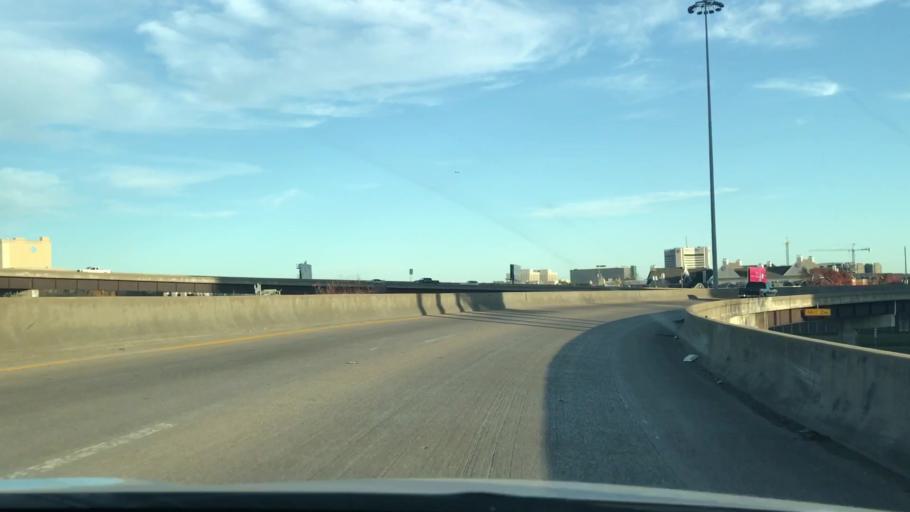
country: US
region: Texas
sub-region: Dallas County
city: Dallas
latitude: 32.7940
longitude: -96.7942
